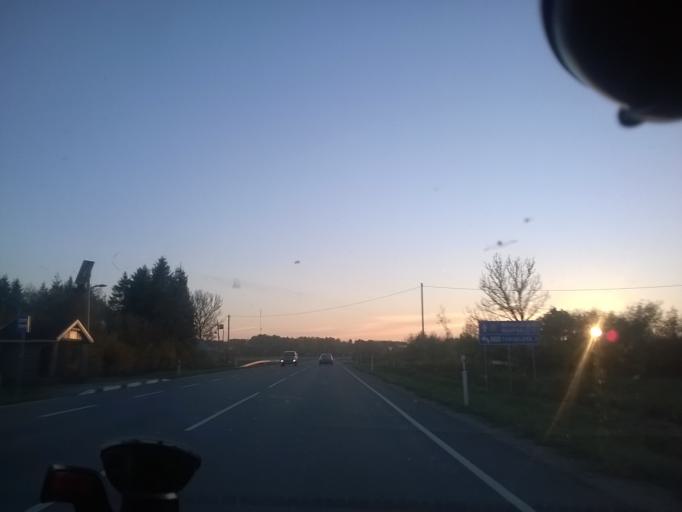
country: EE
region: Laeaene
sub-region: Ridala Parish
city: Uuemoisa
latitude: 58.9631
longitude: 23.8248
